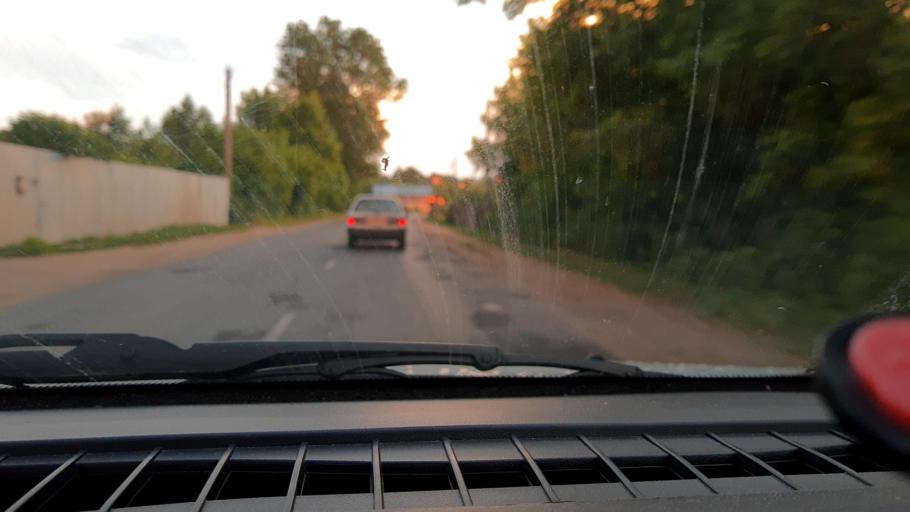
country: RU
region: Nizjnij Novgorod
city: Kstovo
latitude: 56.1312
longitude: 44.0808
